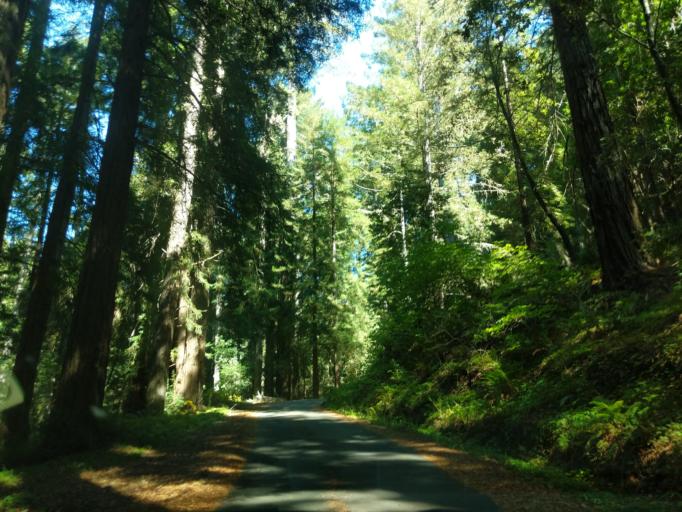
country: US
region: California
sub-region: Sonoma County
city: Monte Rio
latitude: 38.5247
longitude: -123.2395
